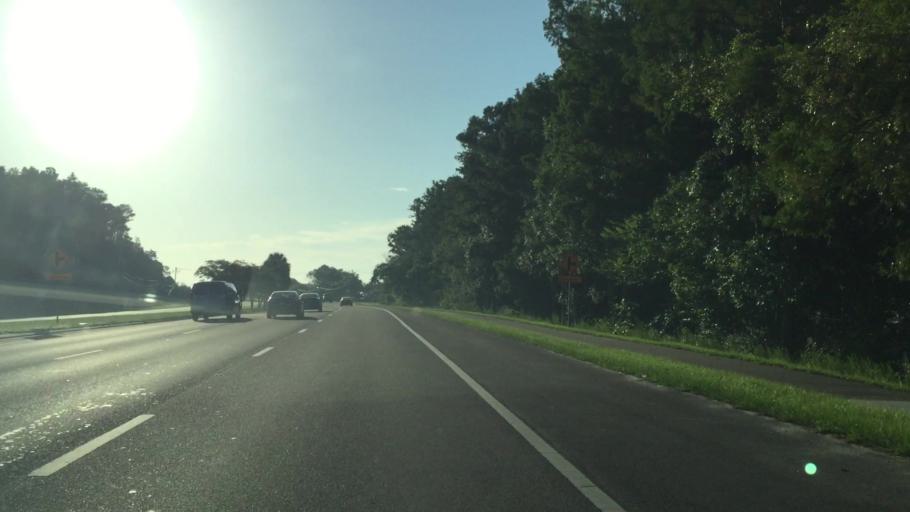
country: US
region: Florida
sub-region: Lee County
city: Villas
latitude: 26.5464
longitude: -81.8342
